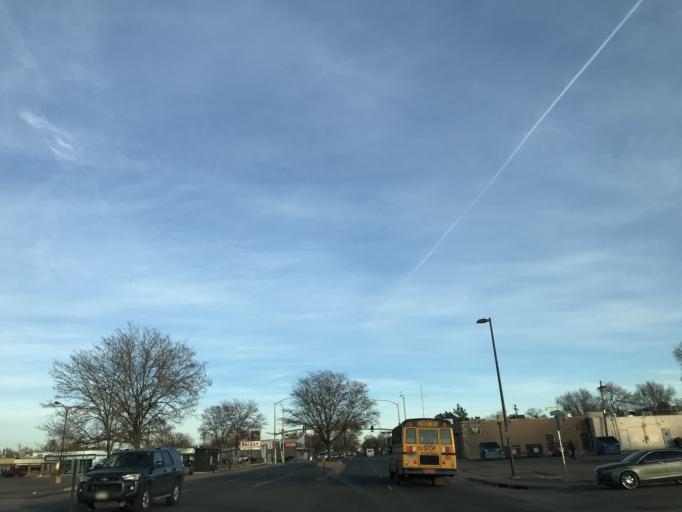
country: US
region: Colorado
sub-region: Adams County
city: Aurora
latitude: 39.7474
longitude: -104.8791
